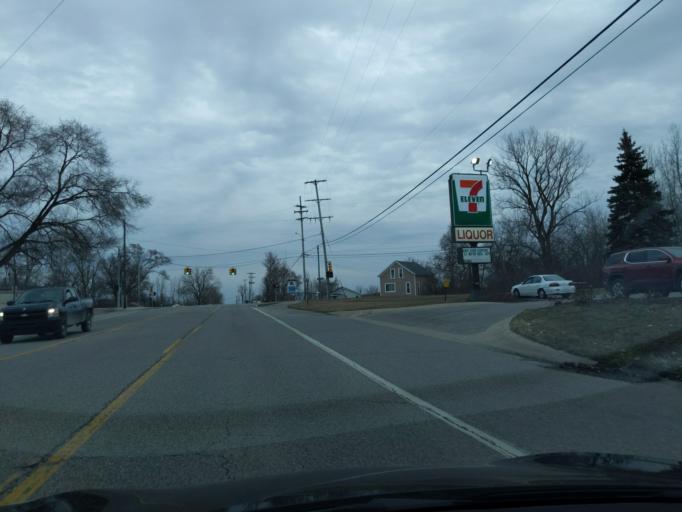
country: US
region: Michigan
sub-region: Bay County
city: Bay City
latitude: 43.6378
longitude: -83.9137
